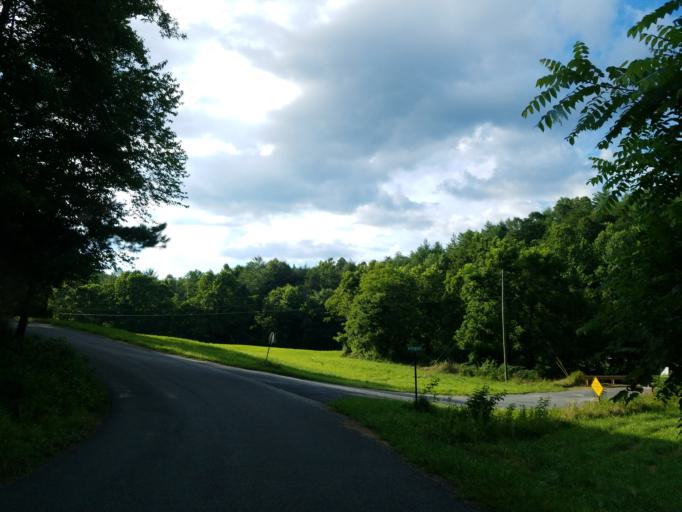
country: US
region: Georgia
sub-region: Gilmer County
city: Ellijay
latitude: 34.6331
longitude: -84.2660
